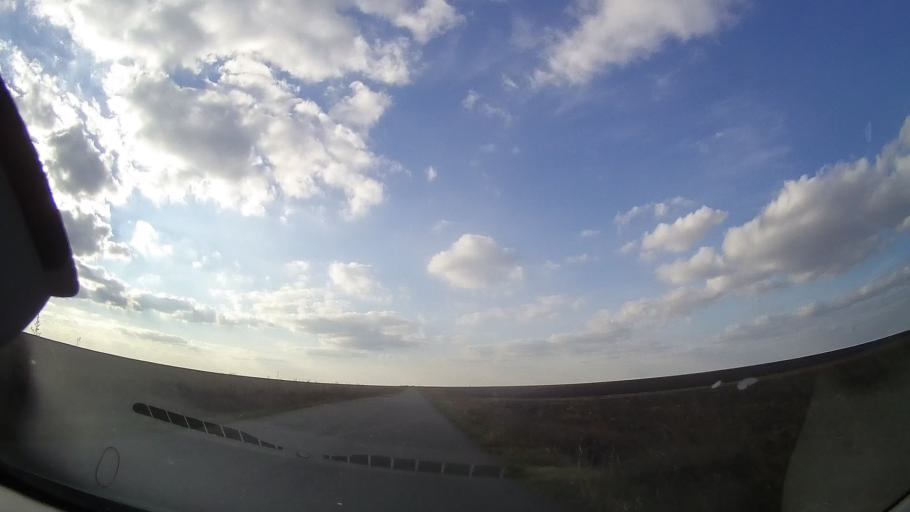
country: RO
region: Constanta
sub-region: Comuna Negru Voda
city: Negru Voda
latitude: 43.8220
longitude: 28.1595
